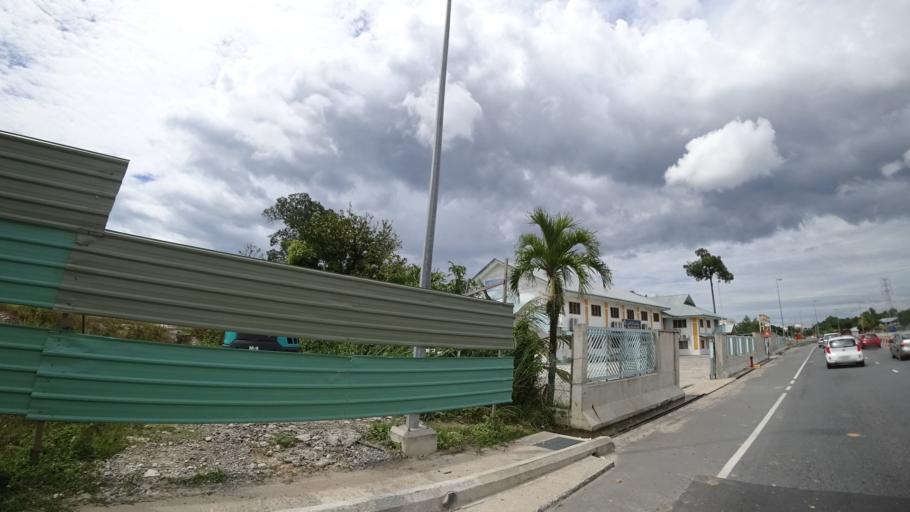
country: BN
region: Brunei and Muara
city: Bandar Seri Begawan
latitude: 4.8833
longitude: 114.8943
